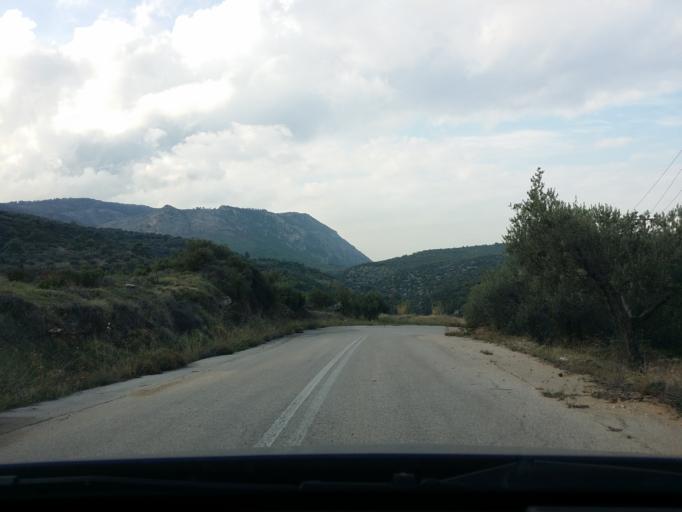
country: GR
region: Attica
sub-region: Nomarchia Anatolikis Attikis
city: Varnavas
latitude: 38.2642
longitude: 23.9664
